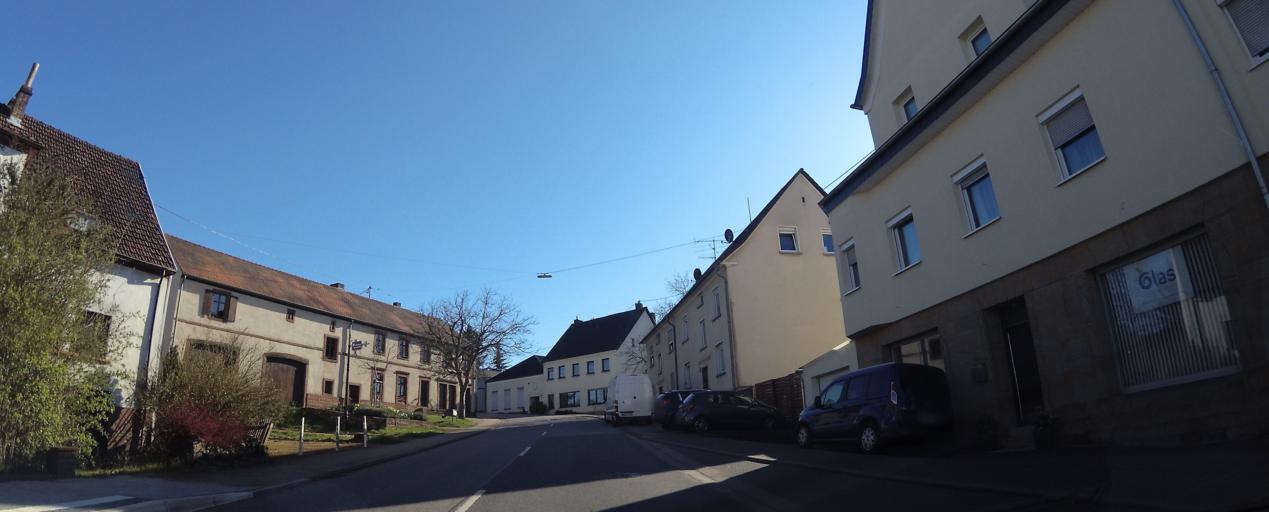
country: DE
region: Saarland
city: Puttlingen
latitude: 49.2989
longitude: 6.8976
